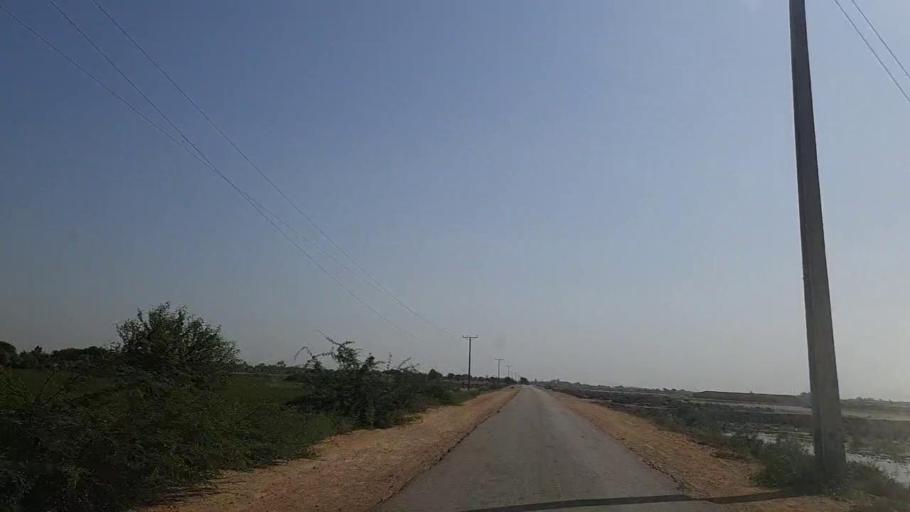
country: PK
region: Sindh
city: Mirpur Batoro
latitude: 24.6322
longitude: 68.2928
